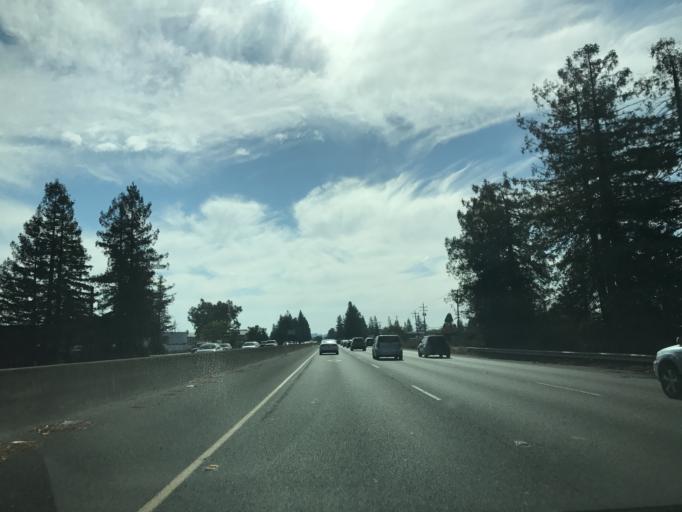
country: US
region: California
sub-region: Sonoma County
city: Roseland
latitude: 38.3841
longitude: -122.7163
